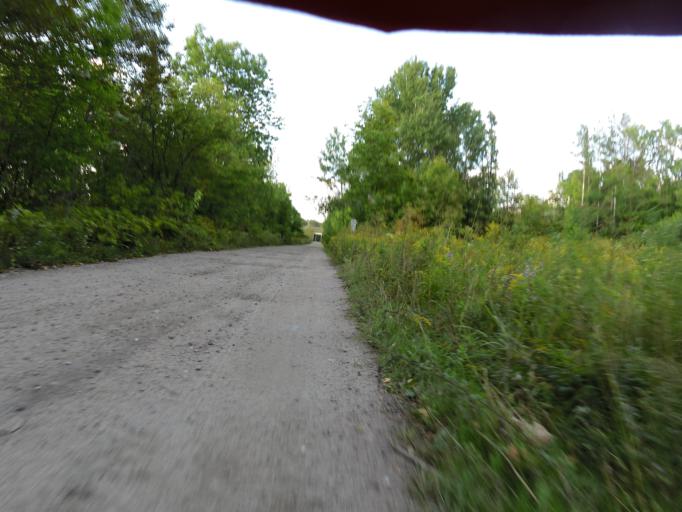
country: CA
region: Quebec
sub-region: Outaouais
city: Maniwaki
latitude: 46.3640
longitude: -75.9848
